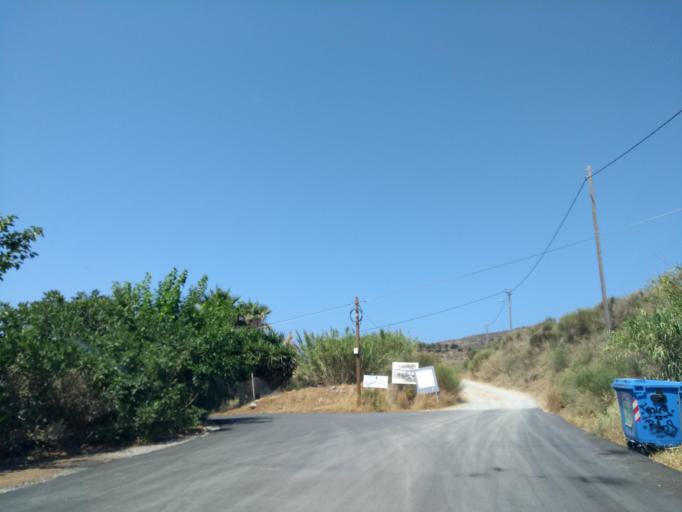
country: GR
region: Crete
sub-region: Nomos Rethymnis
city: Atsipopoulon
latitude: 35.3561
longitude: 24.3685
